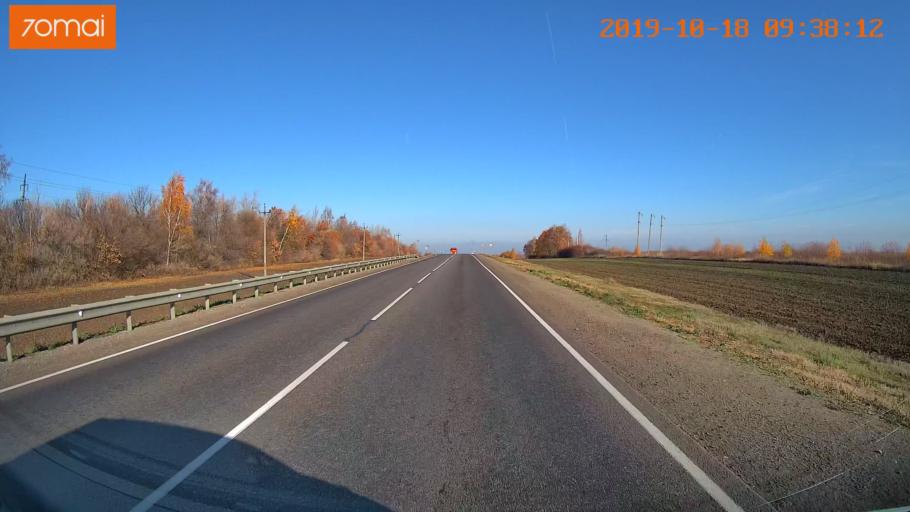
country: RU
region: Tula
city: Yefremov
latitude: 53.2343
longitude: 38.1380
